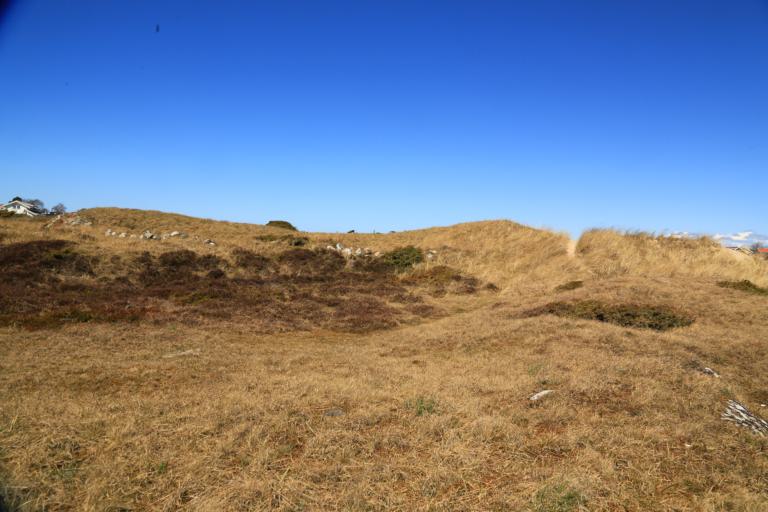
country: SE
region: Halland
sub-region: Varbergs Kommun
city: Traslovslage
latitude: 57.0675
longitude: 12.2643
